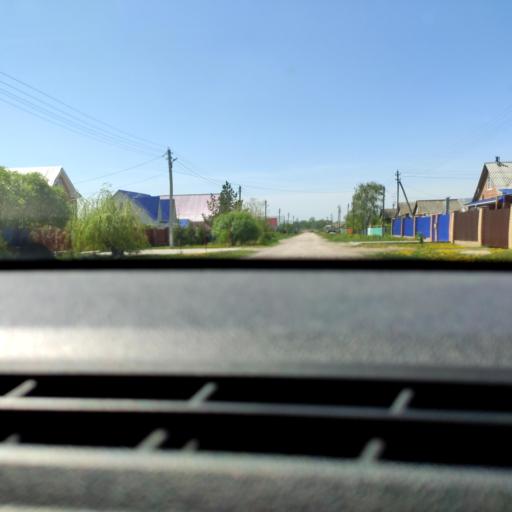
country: RU
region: Samara
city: Tol'yatti
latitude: 53.6755
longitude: 49.4235
